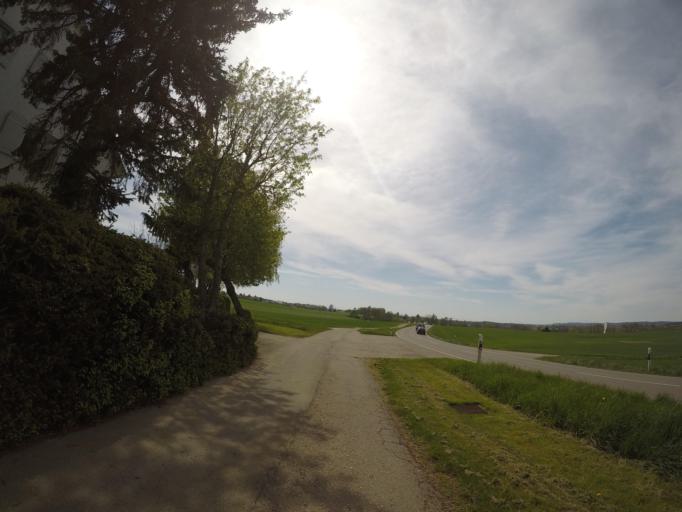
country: DE
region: Baden-Wuerttemberg
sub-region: Tuebingen Region
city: Altshausen
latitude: 47.9476
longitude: 9.5271
